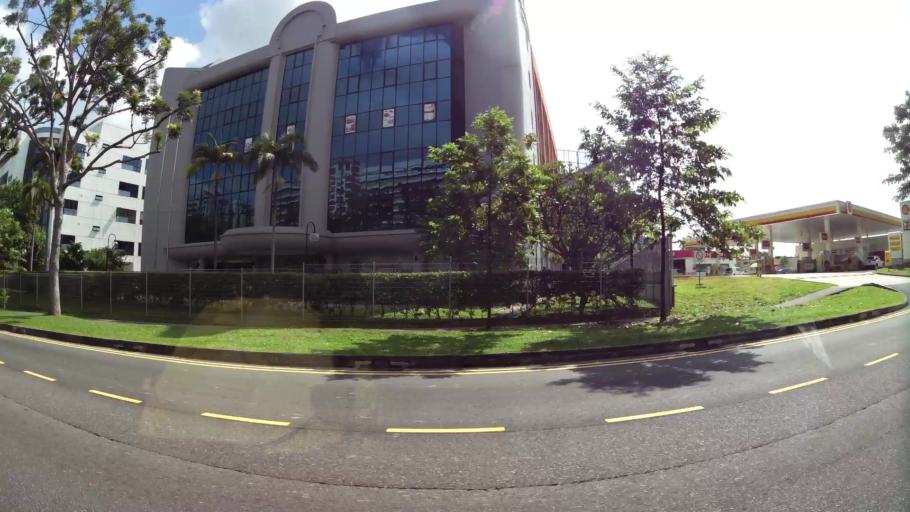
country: SG
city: Singapore
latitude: 1.3497
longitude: 103.8899
